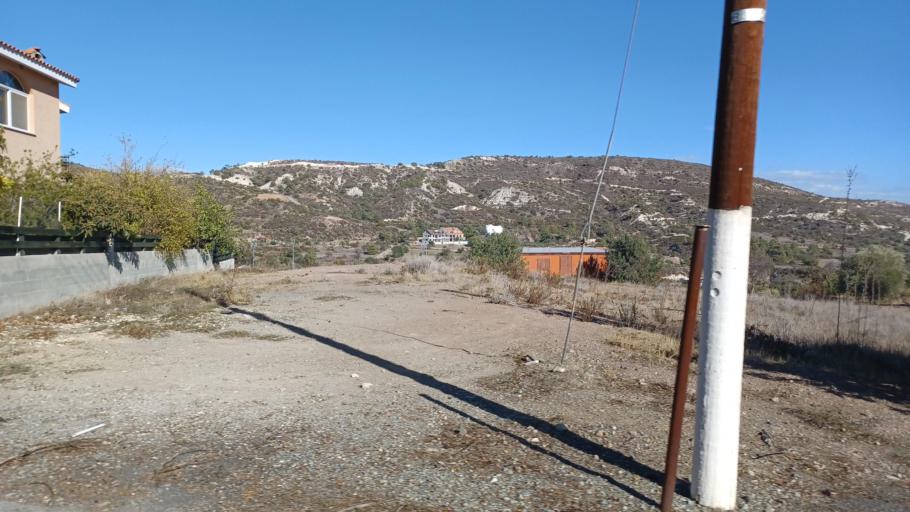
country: CY
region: Limassol
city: Pyrgos
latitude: 34.7821
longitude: 33.2504
